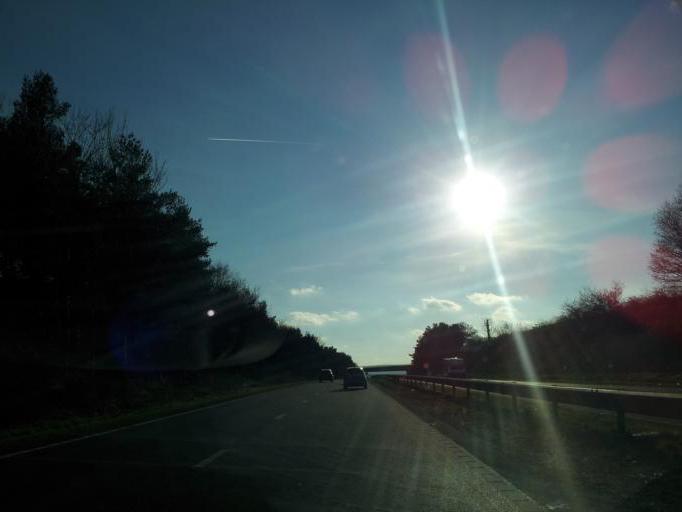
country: GB
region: England
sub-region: Devon
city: Crediton
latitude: 50.7207
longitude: -3.7892
